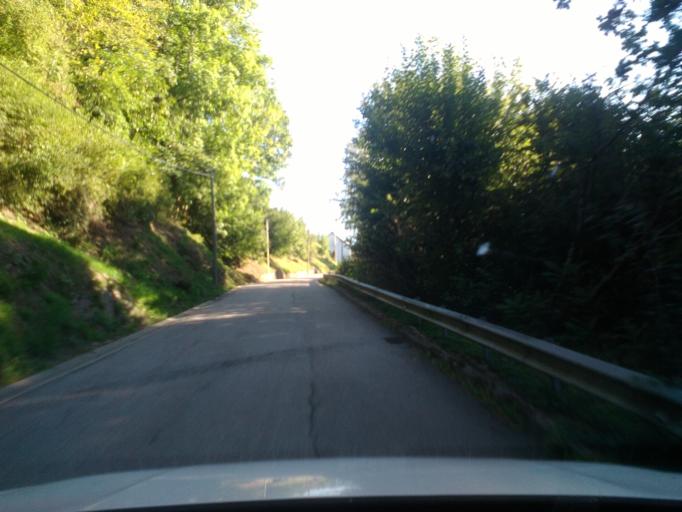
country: FR
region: Lorraine
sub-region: Departement des Vosges
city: Senones
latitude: 48.4331
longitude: 7.0276
